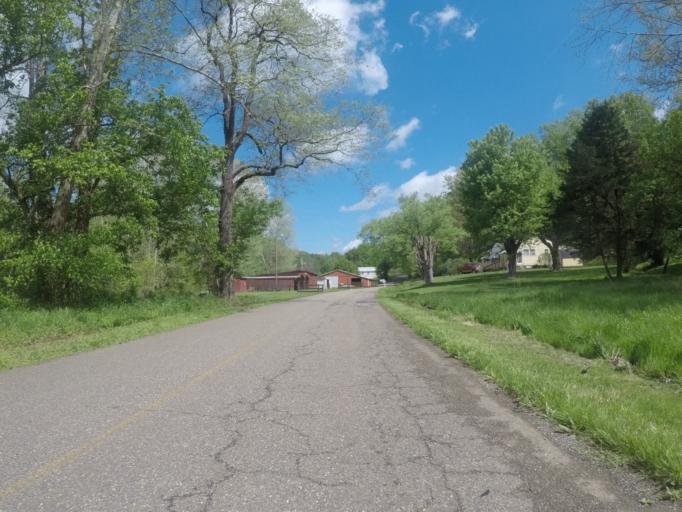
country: US
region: West Virginia
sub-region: Cabell County
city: Huntington
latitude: 38.5247
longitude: -82.4406
